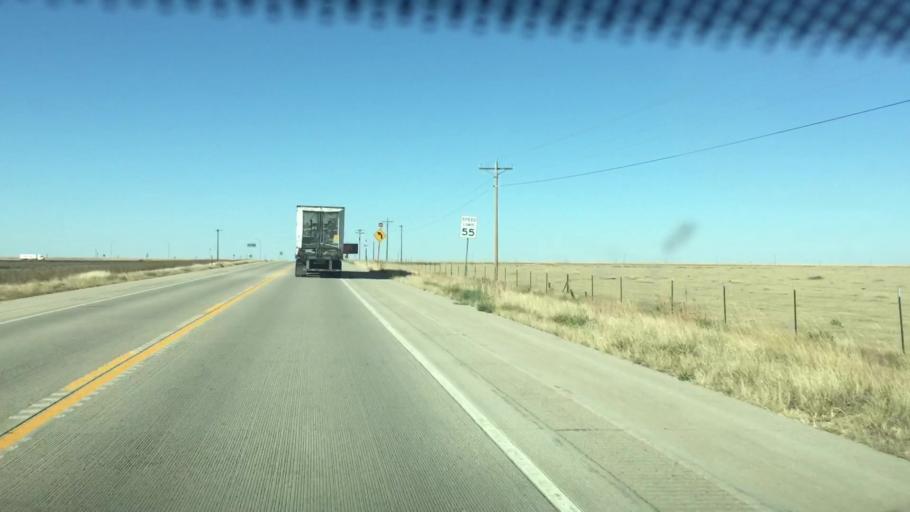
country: US
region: Colorado
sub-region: Kiowa County
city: Eads
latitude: 38.4668
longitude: -102.7307
